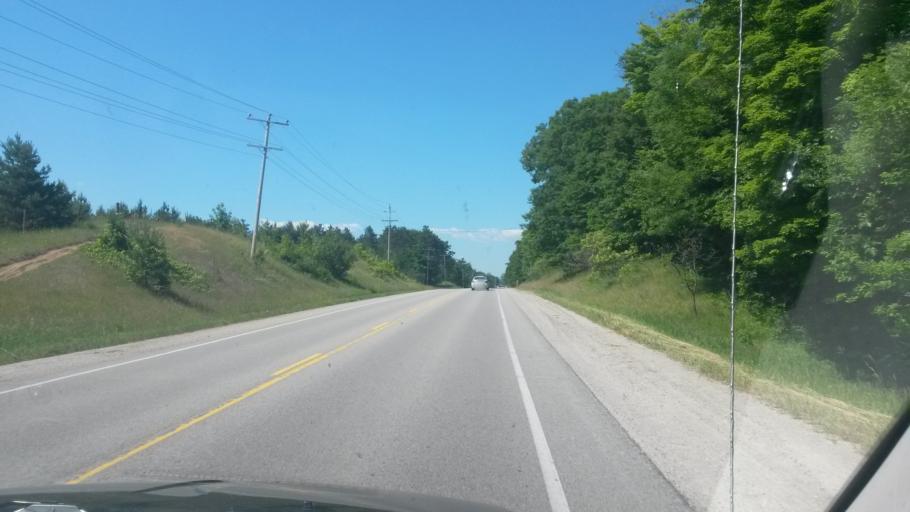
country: CA
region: Ontario
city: Barrie
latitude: 44.5362
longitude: -79.7115
